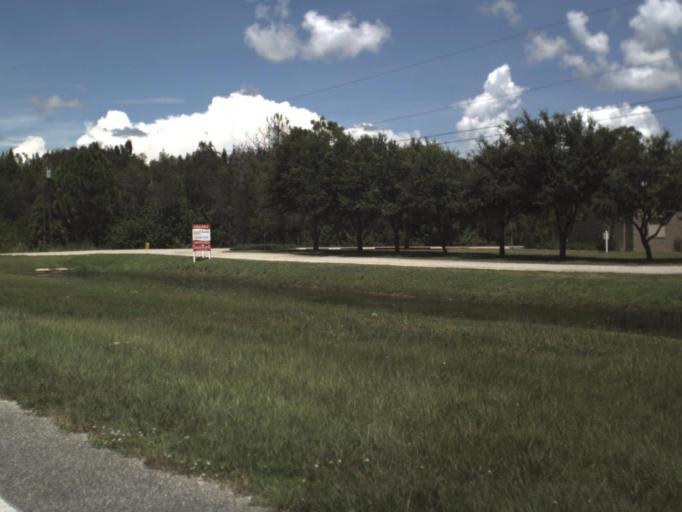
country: US
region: Florida
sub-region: Lee County
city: Burnt Store Marina
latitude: 26.8112
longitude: -81.9576
